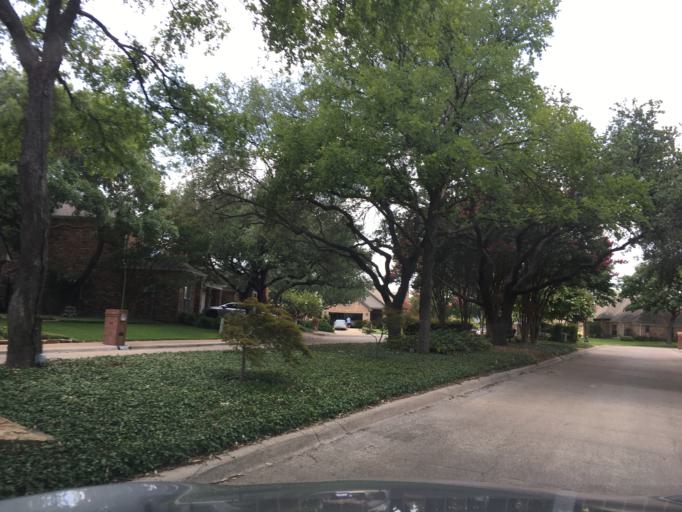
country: US
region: Texas
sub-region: Dallas County
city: Addison
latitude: 32.9480
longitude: -96.8154
